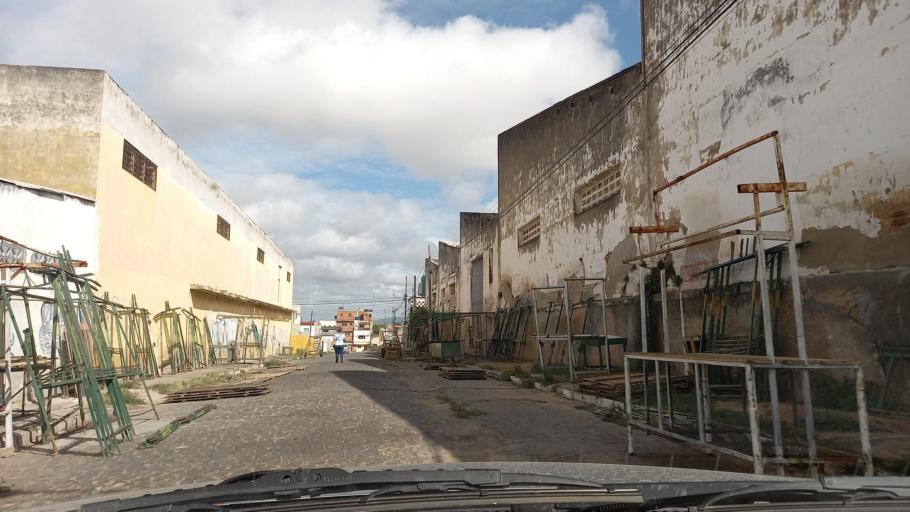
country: BR
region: Pernambuco
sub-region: Caruaru
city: Caruaru
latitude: -8.2873
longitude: -35.9814
